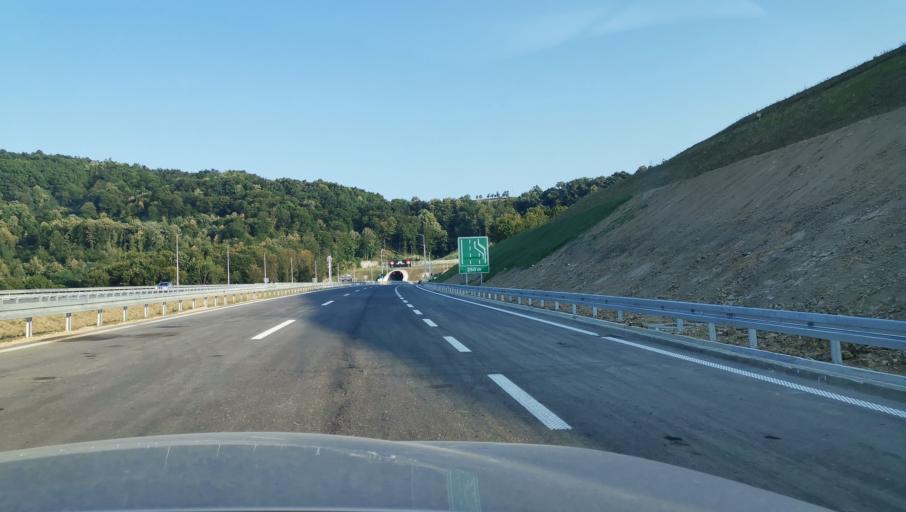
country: RS
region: Central Serbia
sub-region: Kolubarski Okrug
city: Ljig
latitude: 44.2144
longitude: 20.2606
